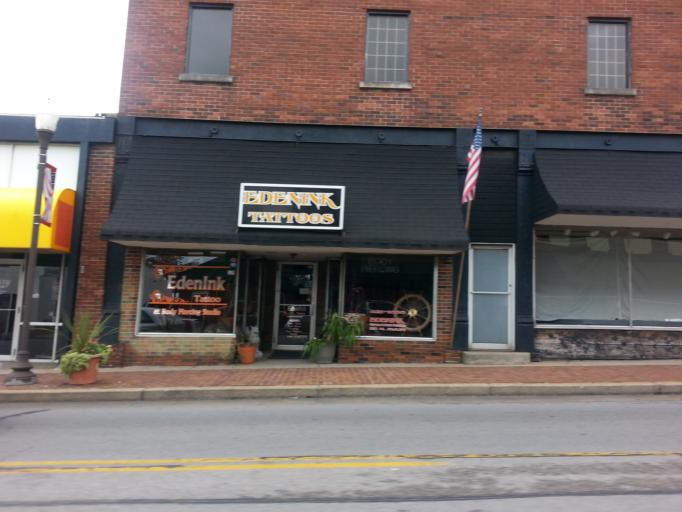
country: US
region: Kentucky
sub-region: Hopkins County
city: Madisonville
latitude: 37.3288
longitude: -87.4988
